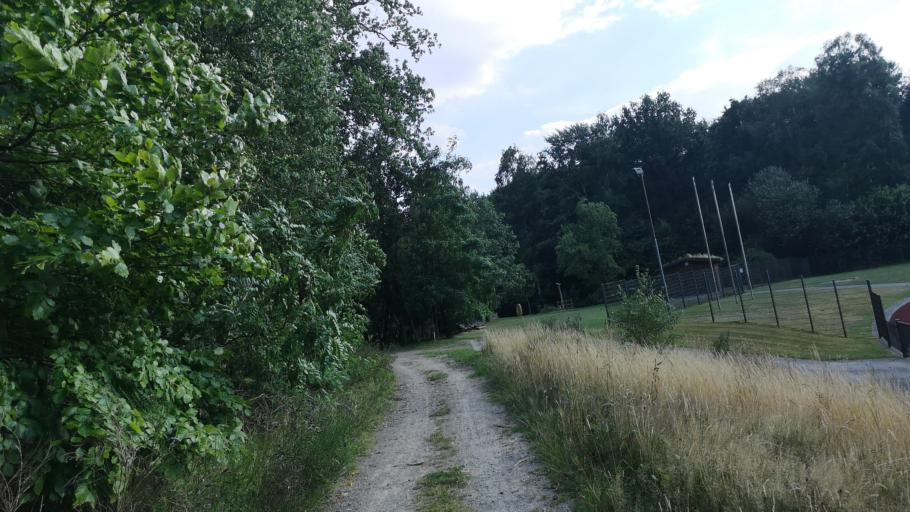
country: DE
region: Lower Saxony
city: Dahlenburg
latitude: 53.2076
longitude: 10.7222
